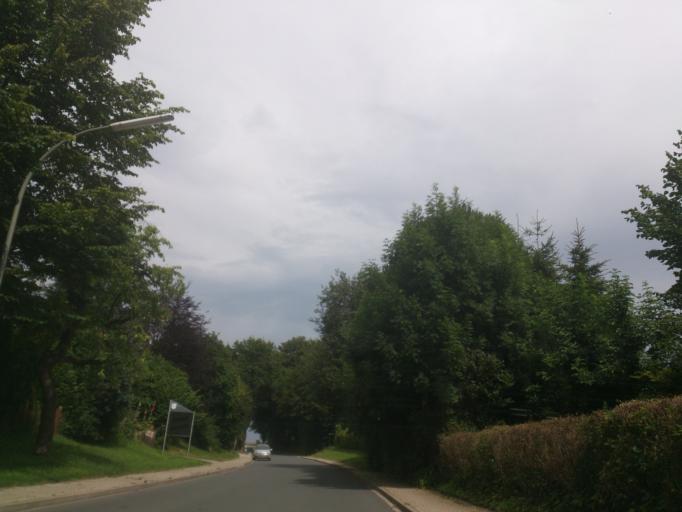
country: DE
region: North Rhine-Westphalia
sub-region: Regierungsbezirk Detmold
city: Wunnenberg
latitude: 51.5186
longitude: 8.7437
